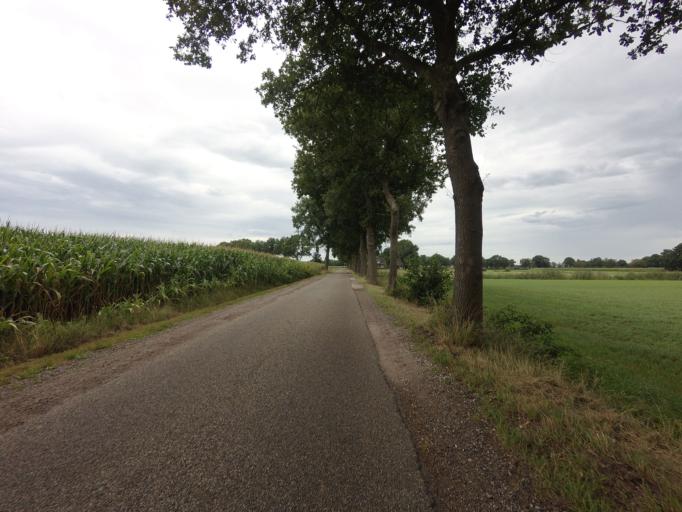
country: NL
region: Overijssel
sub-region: Gemeente Raalte
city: Raalte
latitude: 52.3616
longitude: 6.3539
